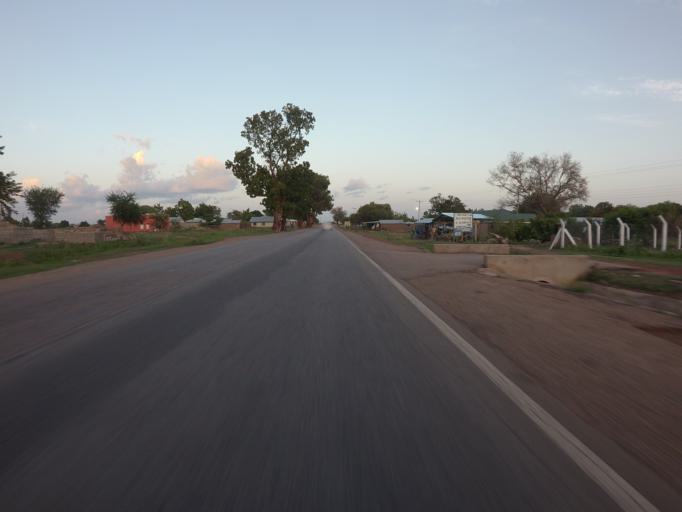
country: GH
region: Upper East
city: Navrongo
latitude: 10.8619
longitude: -1.0334
